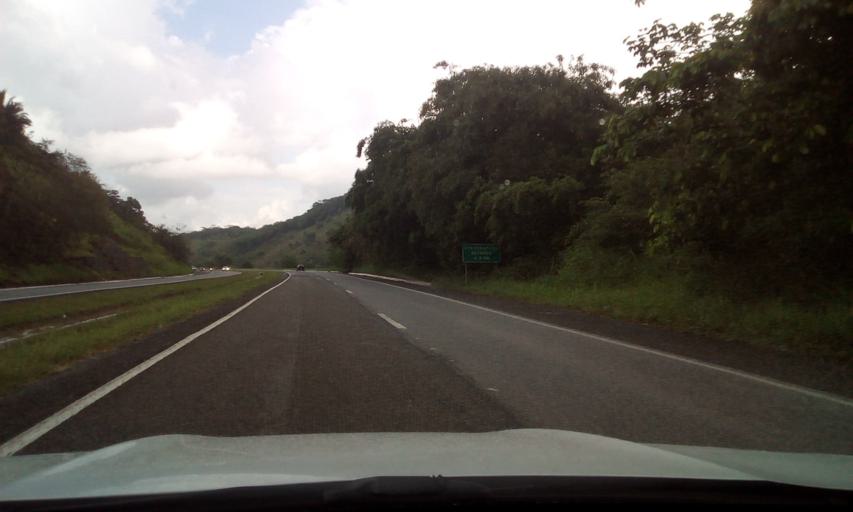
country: BR
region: Pernambuco
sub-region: Cabo De Santo Agostinho
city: Cabo
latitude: -8.2653
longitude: -35.0512
